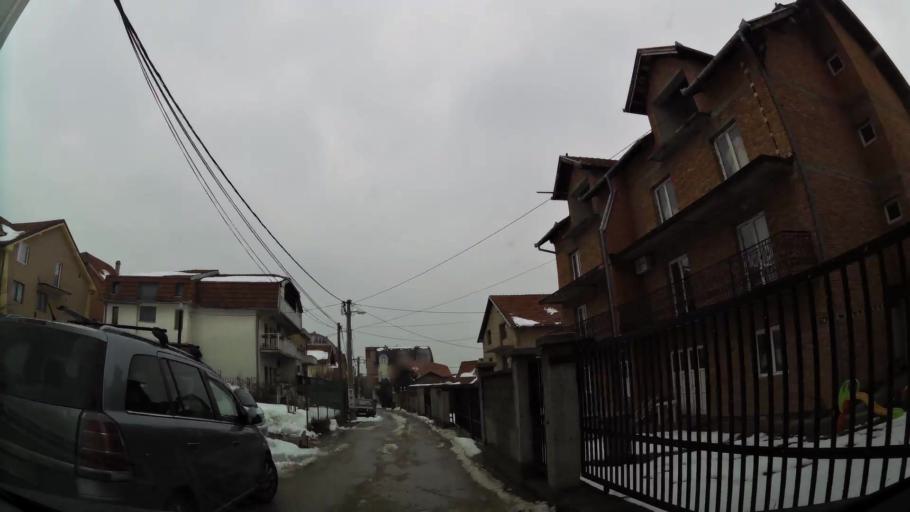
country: RS
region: Central Serbia
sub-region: Belgrade
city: Zvezdara
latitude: 44.7685
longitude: 20.5103
